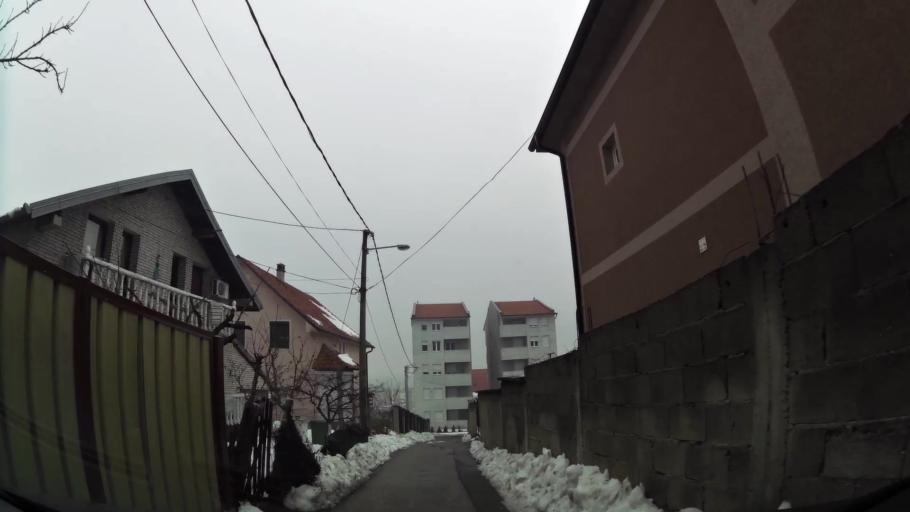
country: RS
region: Central Serbia
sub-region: Belgrade
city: Zvezdara
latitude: 44.7849
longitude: 20.5266
